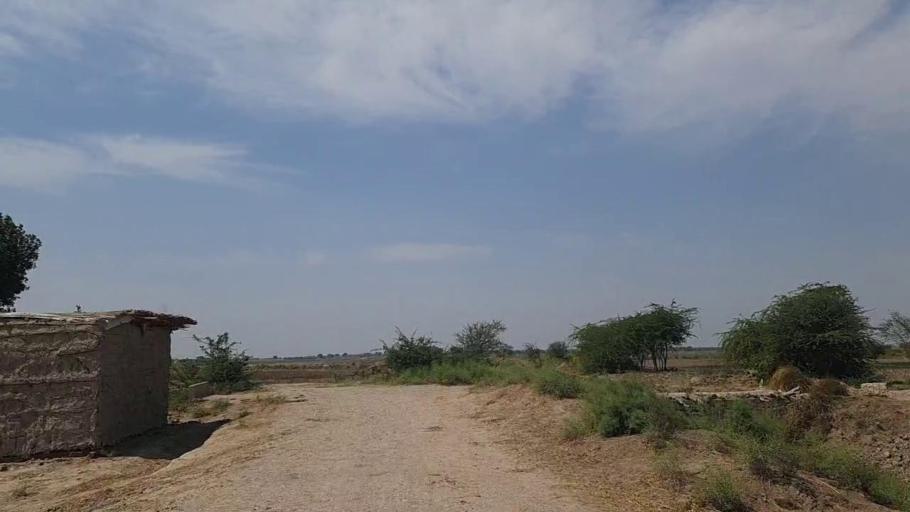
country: PK
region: Sindh
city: Jati
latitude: 24.5373
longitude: 68.3050
